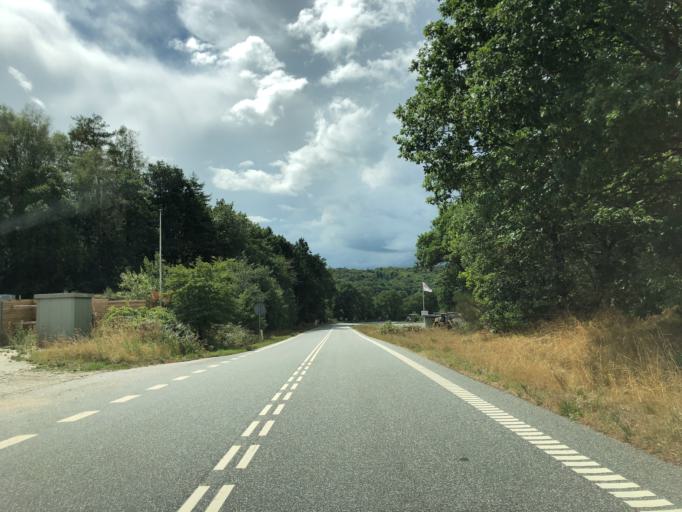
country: DK
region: Central Jutland
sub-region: Silkeborg Kommune
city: Silkeborg
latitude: 56.1417
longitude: 9.4218
